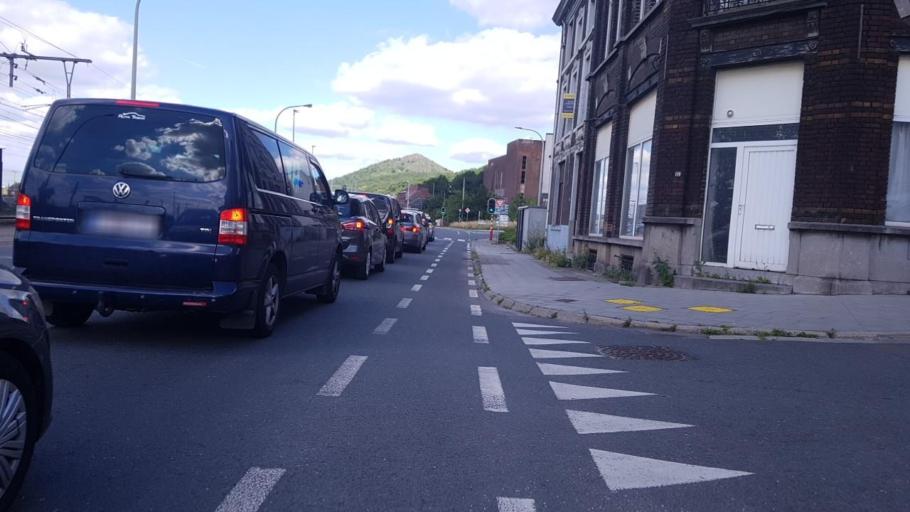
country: BE
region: Wallonia
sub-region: Province du Hainaut
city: Charleroi
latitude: 50.3925
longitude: 4.4753
